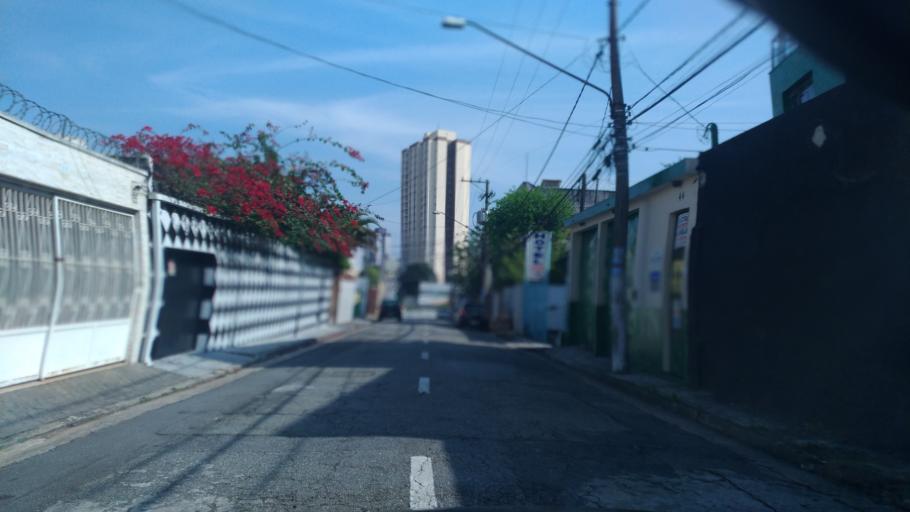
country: BR
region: Sao Paulo
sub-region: Sao Bernardo Do Campo
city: Sao Bernardo do Campo
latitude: -23.6908
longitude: -46.5662
